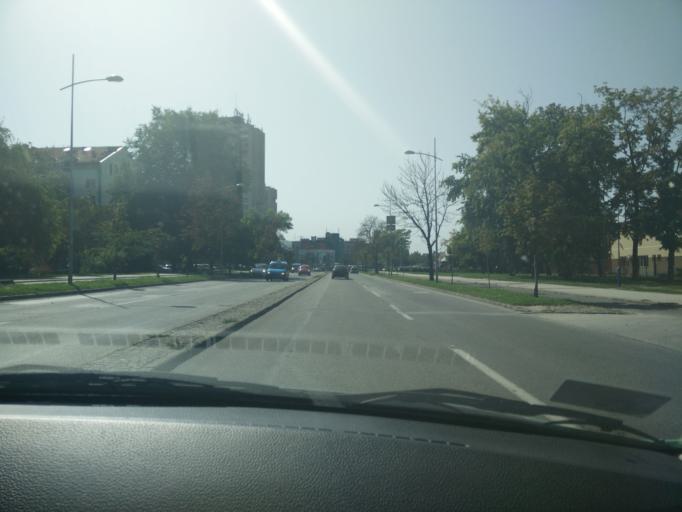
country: RS
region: Autonomna Pokrajina Vojvodina
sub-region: Juznobacki Okrug
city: Novi Sad
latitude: 45.2656
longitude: 19.8337
